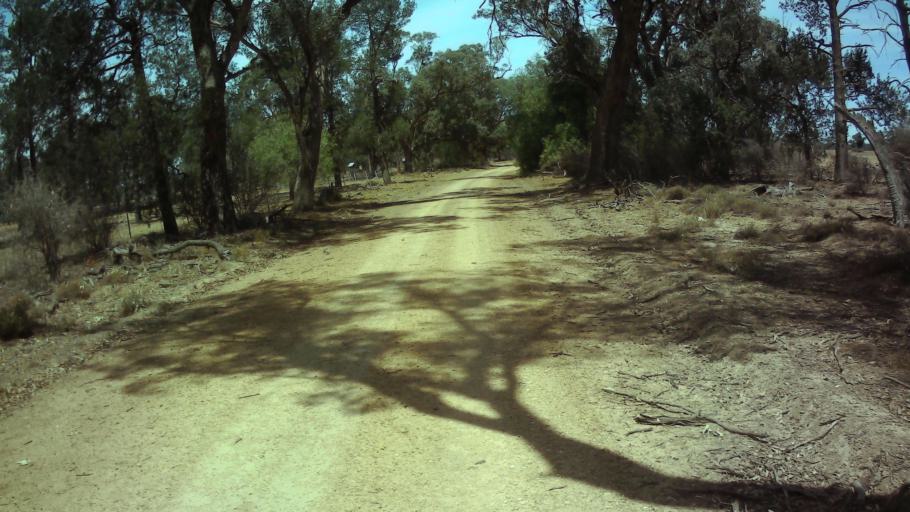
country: AU
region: New South Wales
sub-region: Weddin
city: Grenfell
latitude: -34.0306
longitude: 147.9346
